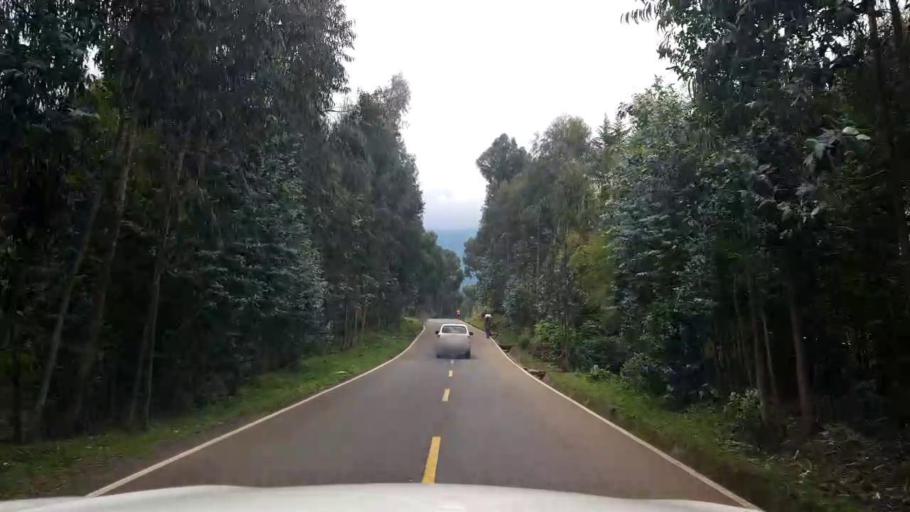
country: RW
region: Northern Province
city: Musanze
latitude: -1.4383
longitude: 29.5471
